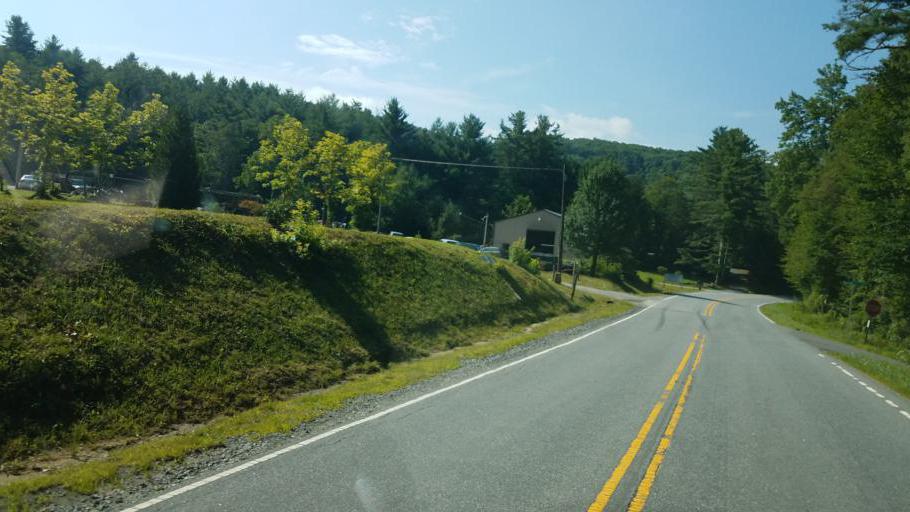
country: US
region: North Carolina
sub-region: Avery County
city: Newland
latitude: 35.9906
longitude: -81.8917
